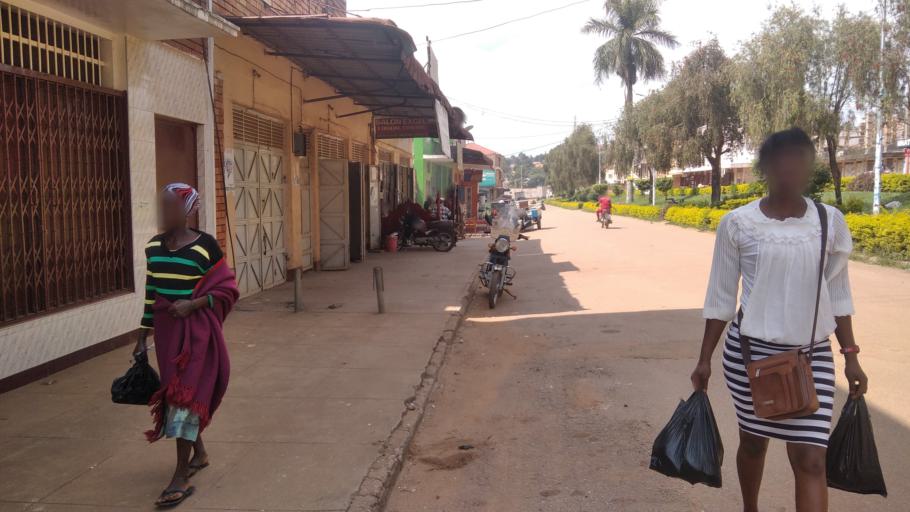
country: UG
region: Central Region
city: Masaka
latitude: -0.3454
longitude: 31.7398
